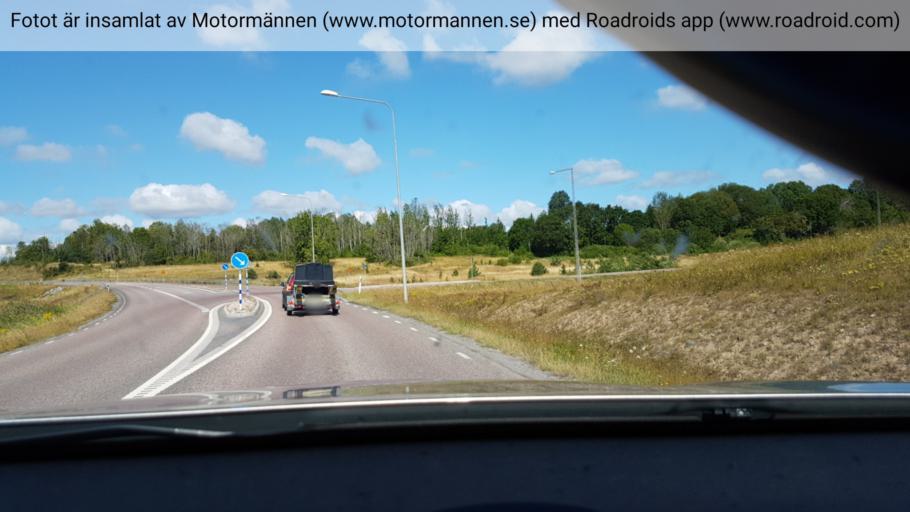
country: SE
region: Stockholm
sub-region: Norrtalje Kommun
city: Norrtalje
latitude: 59.7431
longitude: 18.6899
